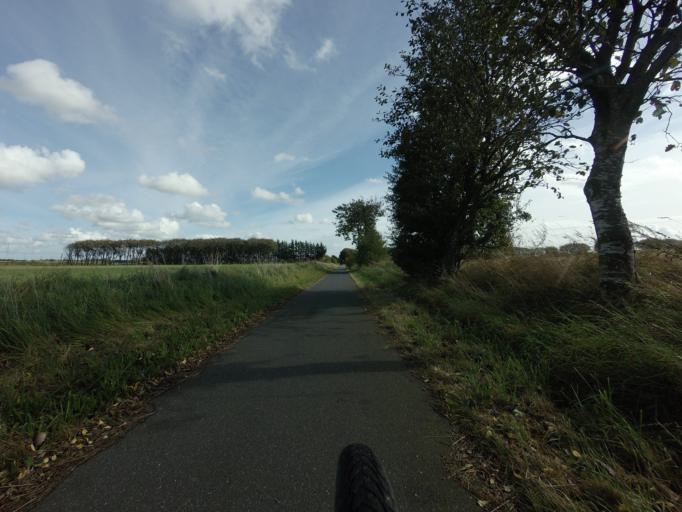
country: DK
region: Central Jutland
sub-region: Favrskov Kommune
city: Ulstrup
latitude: 56.5002
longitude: 9.7186
